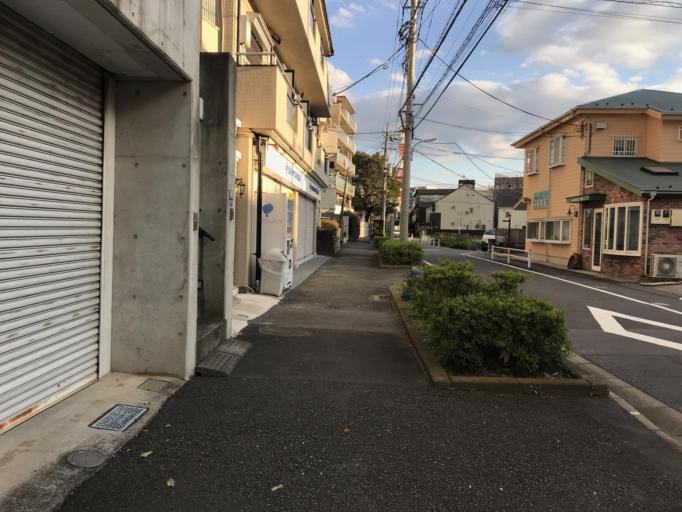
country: JP
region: Kanagawa
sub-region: Kawasaki-shi
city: Kawasaki
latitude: 35.5743
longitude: 139.6856
